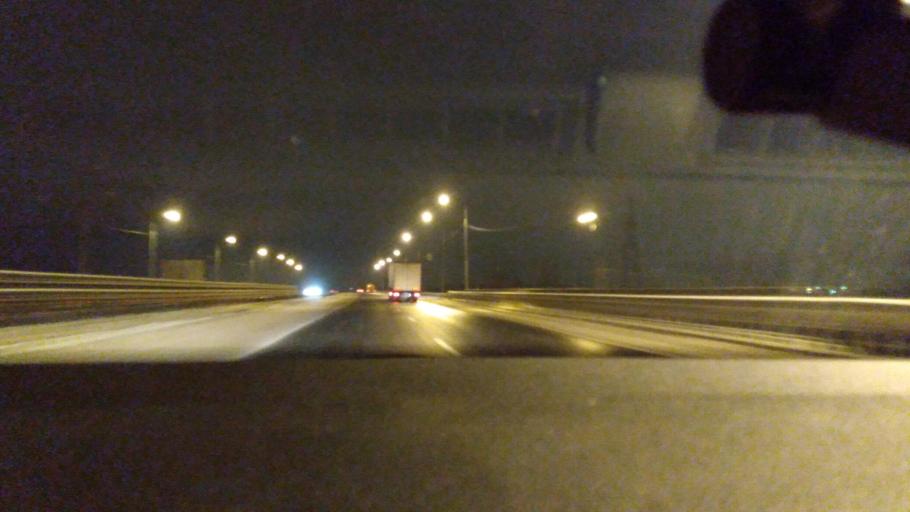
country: RU
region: Moskovskaya
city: Raduzhnyy
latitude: 55.1321
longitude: 38.7764
